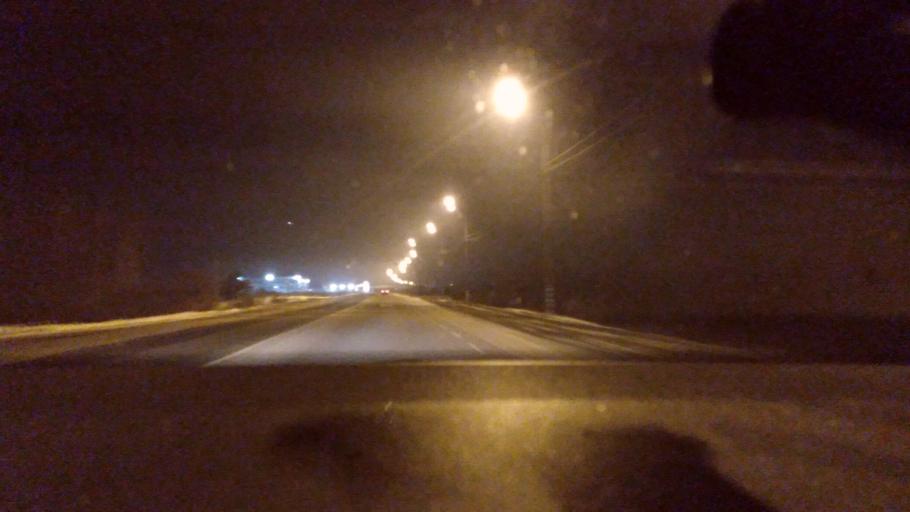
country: RU
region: Moskovskaya
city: Il'inskiy Pogost
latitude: 55.4888
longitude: 38.8822
